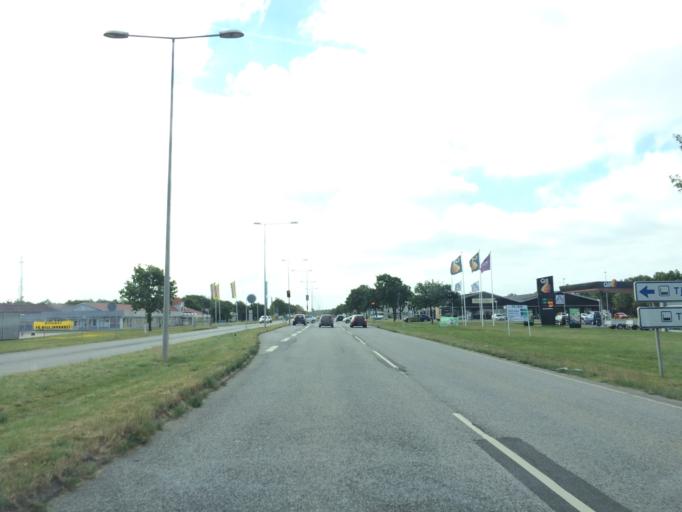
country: DK
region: Central Jutland
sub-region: Herning Kommune
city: Snejbjerg
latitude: 56.1545
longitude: 8.9305
